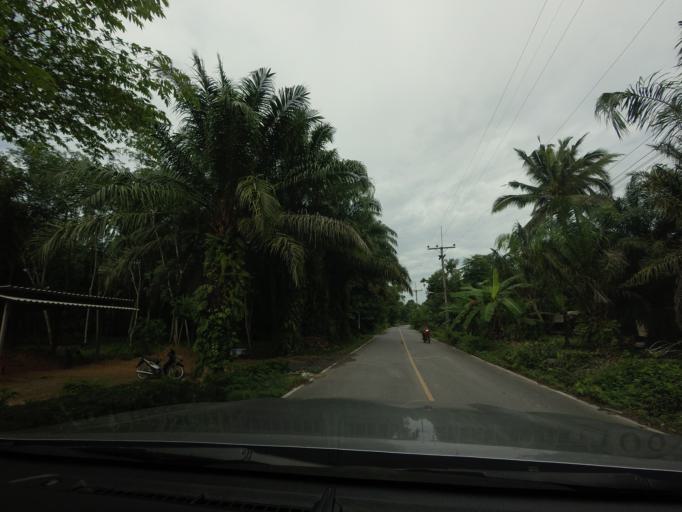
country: TH
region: Nakhon Si Thammarat
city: Phra Phrom
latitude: 8.2829
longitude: 99.9297
